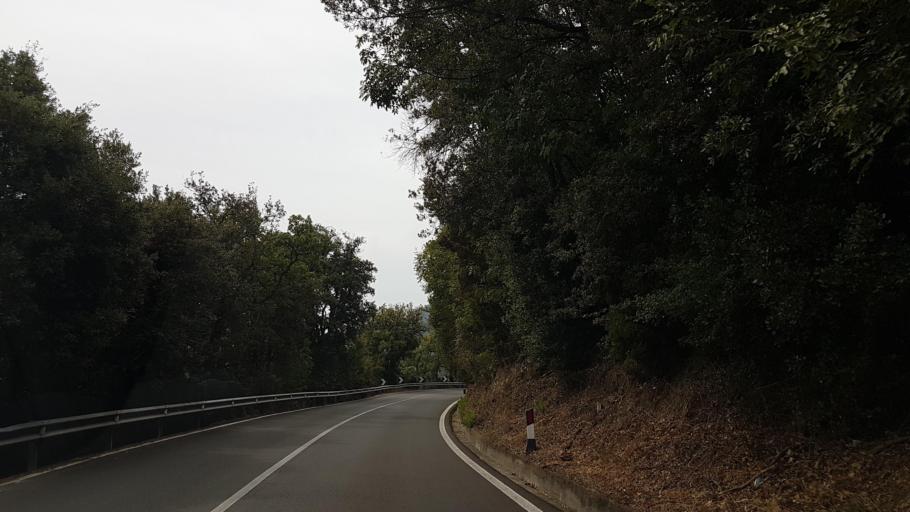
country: IT
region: Liguria
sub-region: Provincia di Genova
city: Moneglia
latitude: 44.2575
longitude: 9.4886
